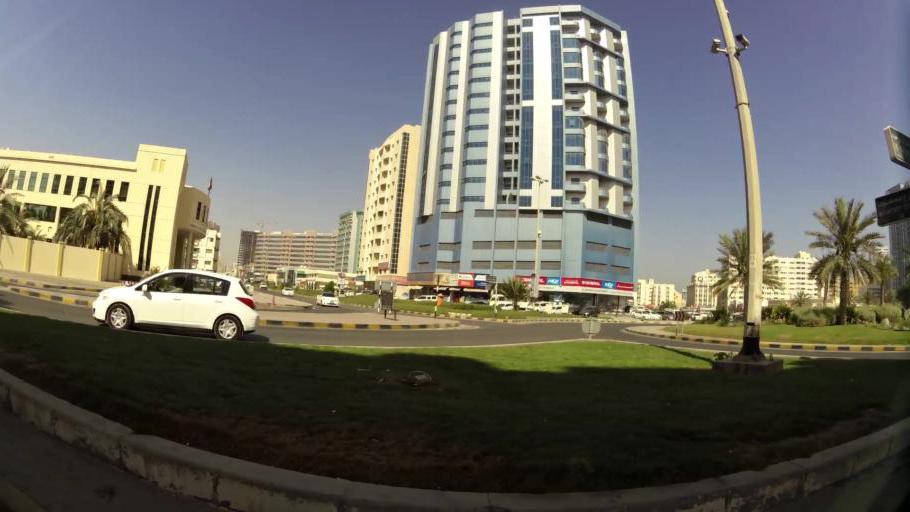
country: AE
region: Ajman
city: Ajman
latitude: 25.4097
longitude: 55.4468
